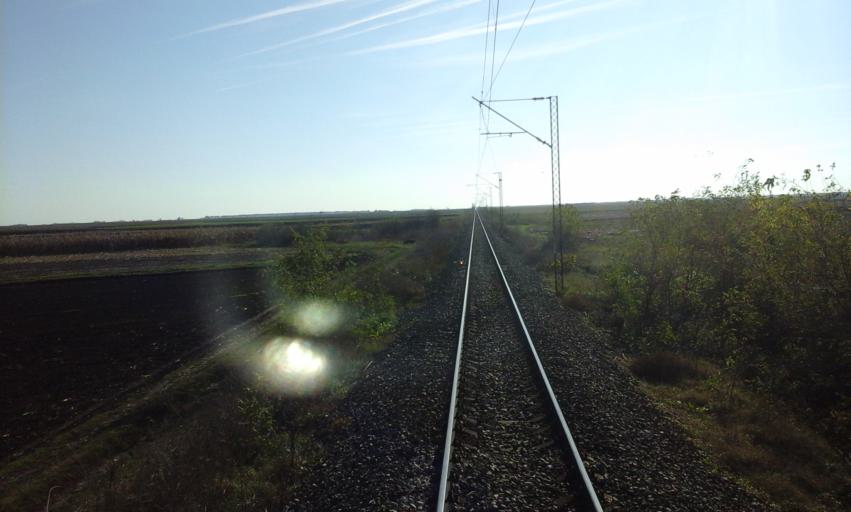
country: RS
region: Autonomna Pokrajina Vojvodina
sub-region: Severnobacki Okrug
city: Backa Topola
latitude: 45.9245
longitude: 19.6659
